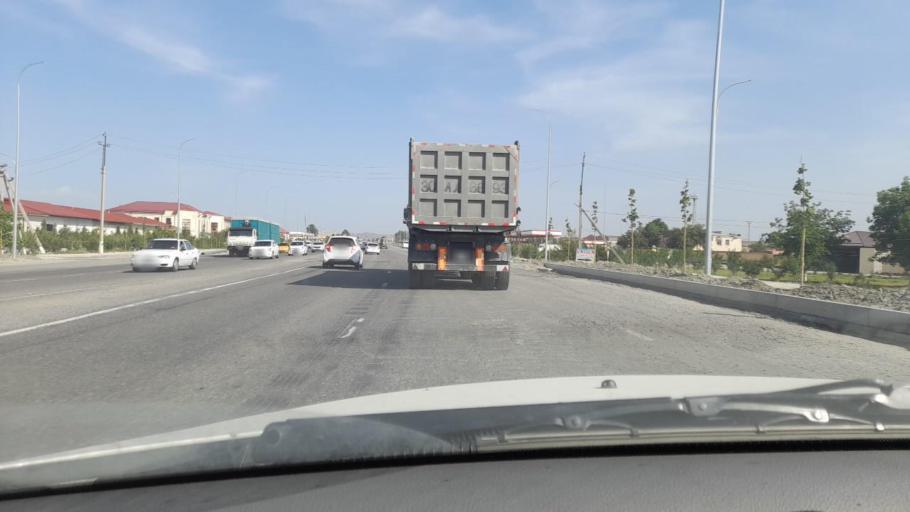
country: UZ
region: Samarqand
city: Daxbet
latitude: 39.7311
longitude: 66.9371
